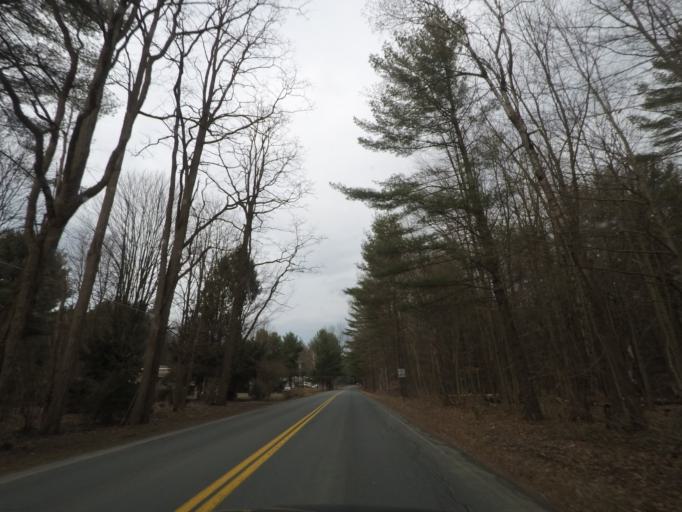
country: US
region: New York
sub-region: Saratoga County
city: Stillwater
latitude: 42.9319
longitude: -73.5017
